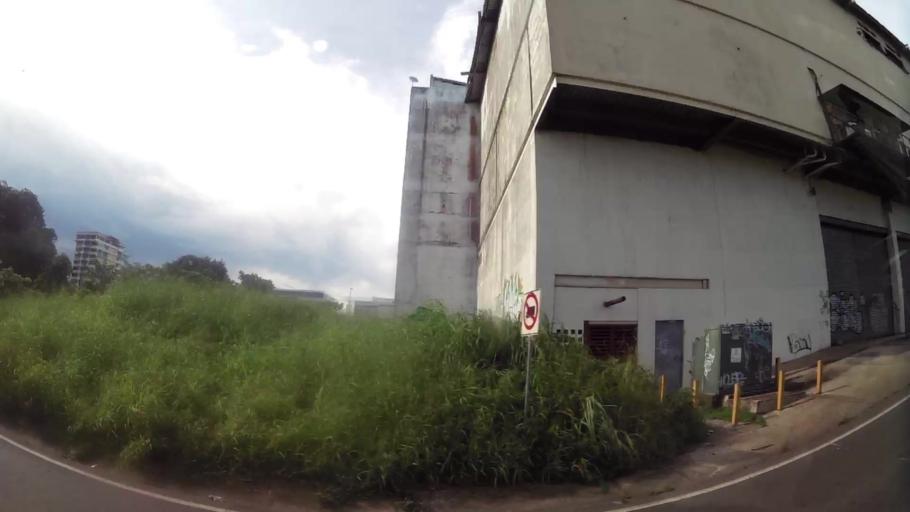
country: PA
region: Panama
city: La Chorrera
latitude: 8.8875
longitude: -79.7716
